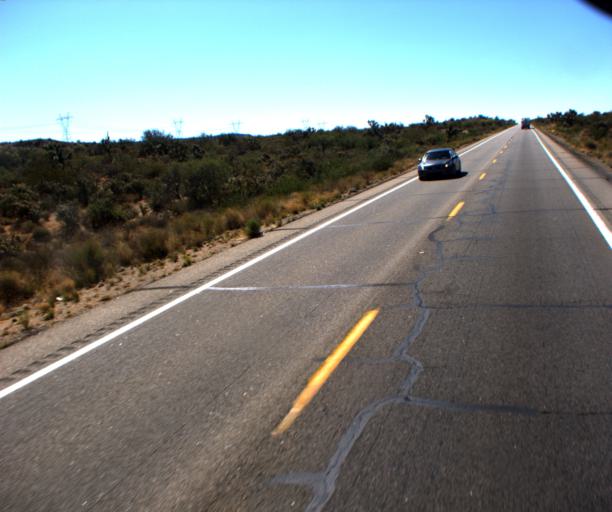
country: US
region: Arizona
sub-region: Yavapai County
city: Bagdad
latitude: 34.3546
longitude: -113.1674
